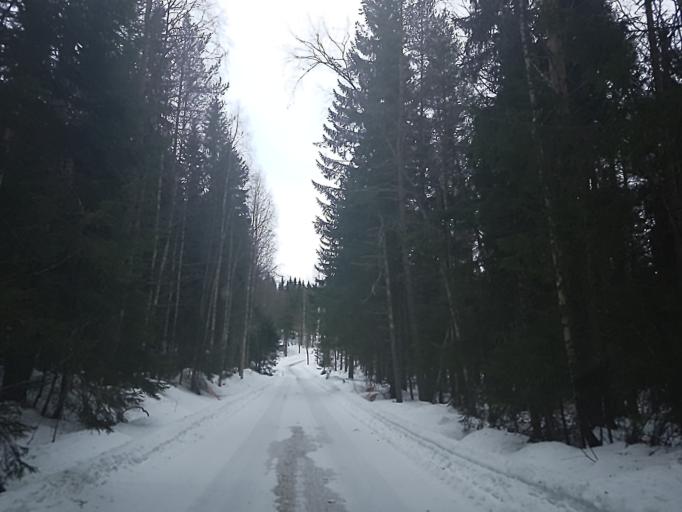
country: FI
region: Northern Savo
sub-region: Koillis-Savo
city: Kaavi
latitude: 62.9788
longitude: 28.7562
